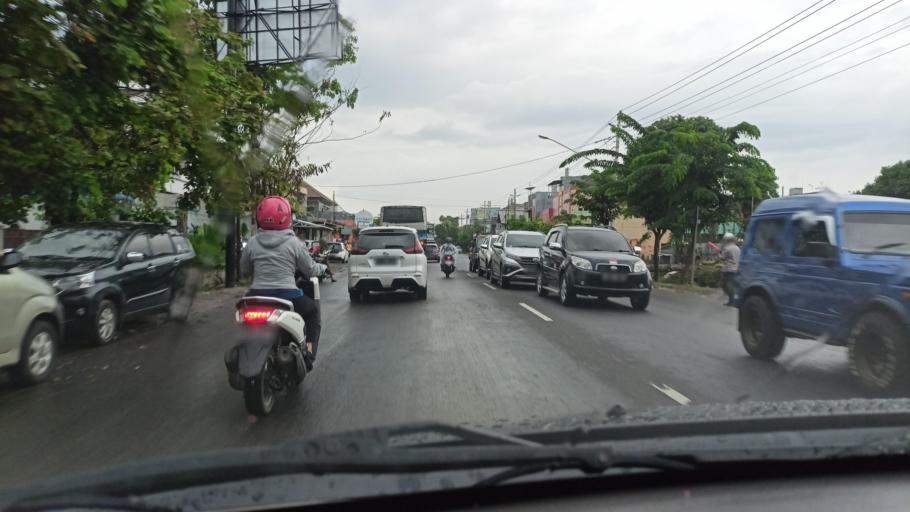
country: ID
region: Central Java
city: Surakarta
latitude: -7.5542
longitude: 110.8272
